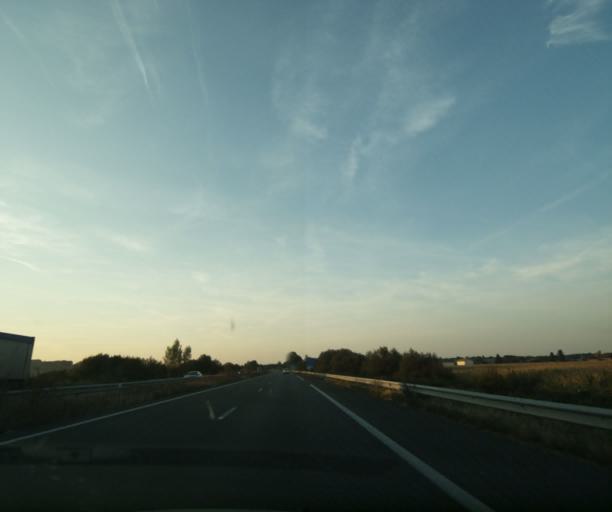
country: FR
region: Aquitaine
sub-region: Departement du Lot-et-Garonne
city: Damazan
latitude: 44.3303
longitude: 0.2571
